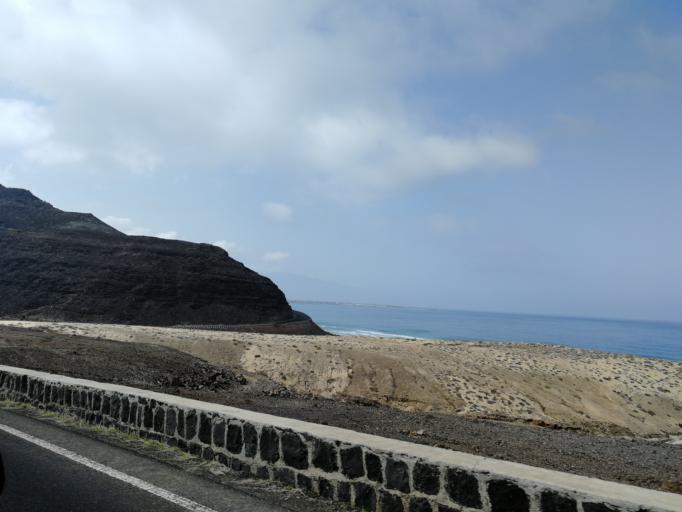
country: CV
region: Sao Vicente
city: Mindelo
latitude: 16.8623
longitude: -24.8934
